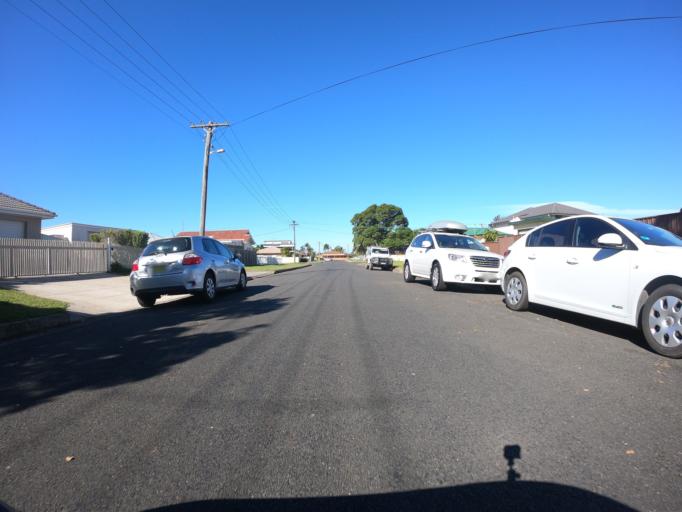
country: AU
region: New South Wales
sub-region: Wollongong
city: Bulli
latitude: -34.3122
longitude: 150.9259
